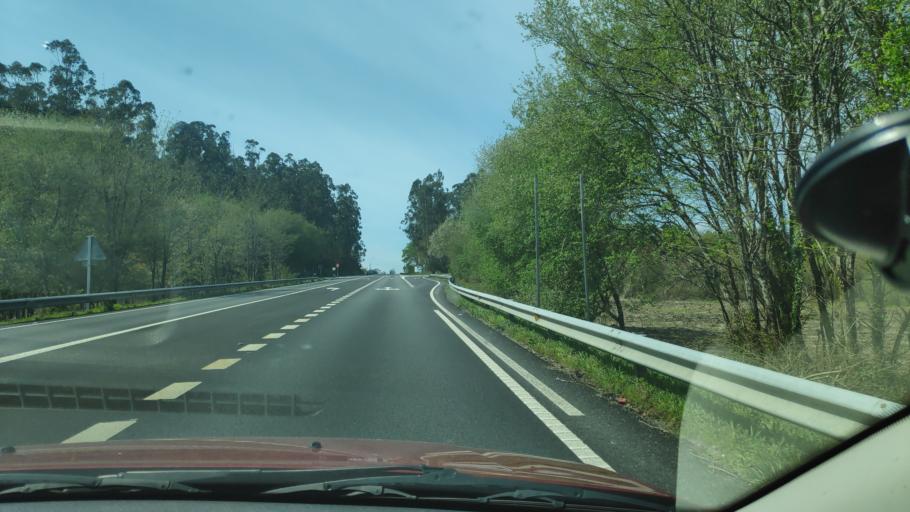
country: ES
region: Galicia
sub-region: Provincia da Coruna
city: Ames
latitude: 42.8775
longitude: -8.6748
